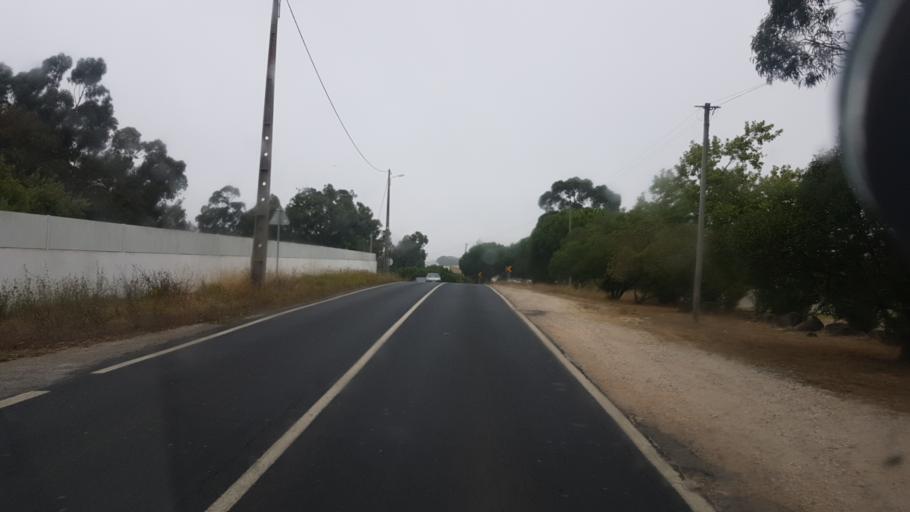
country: PT
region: Lisbon
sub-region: Sintra
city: Sintra
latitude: 38.8188
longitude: -9.3669
